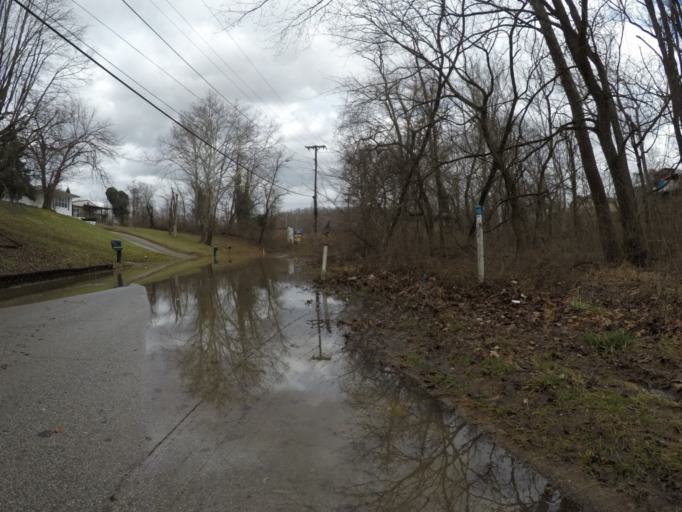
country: US
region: West Virginia
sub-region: Cabell County
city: Pea Ridge
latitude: 38.4094
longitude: -82.3827
